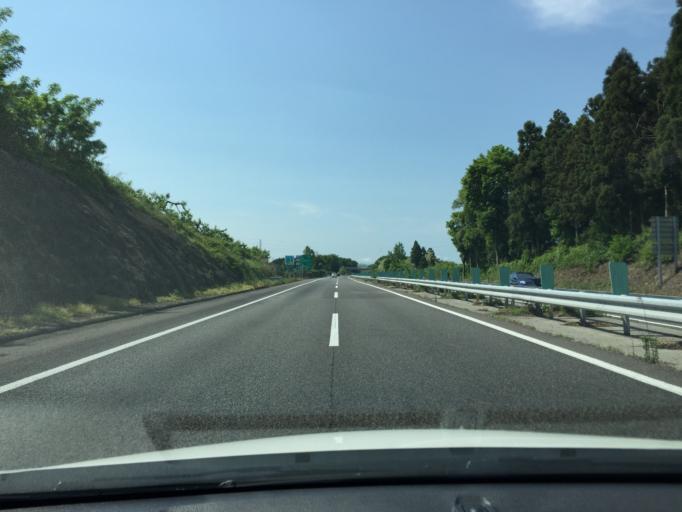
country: JP
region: Fukushima
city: Sukagawa
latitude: 37.2781
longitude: 140.3506
